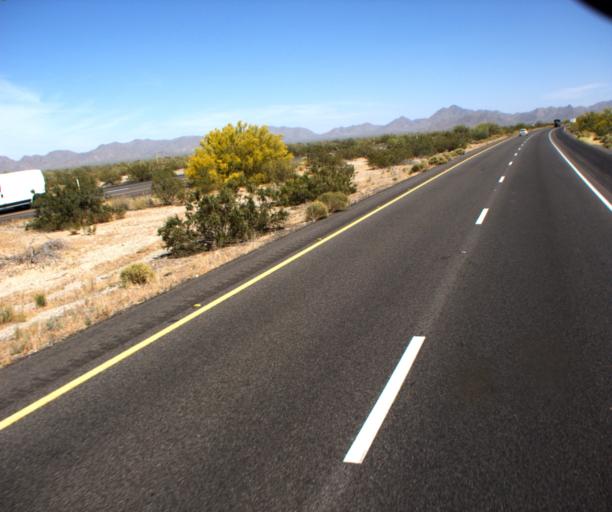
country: US
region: Arizona
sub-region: Maricopa County
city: Gila Bend
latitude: 32.9072
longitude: -112.5395
